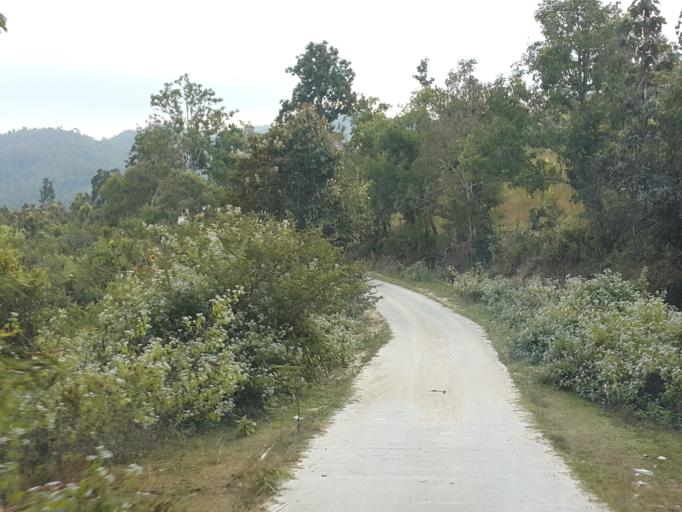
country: TH
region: Chiang Mai
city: Om Koi
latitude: 17.8069
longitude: 98.3189
